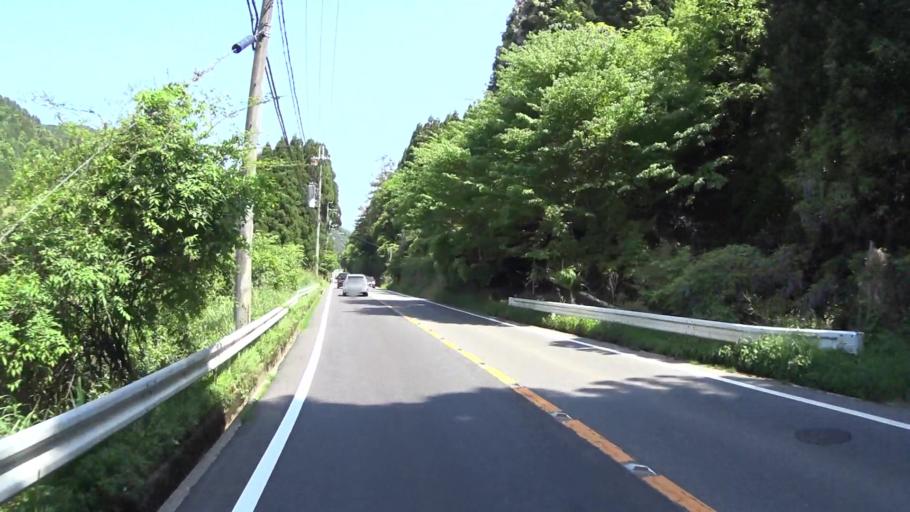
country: JP
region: Shiga Prefecture
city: Kitahama
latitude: 35.1235
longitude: 135.8340
